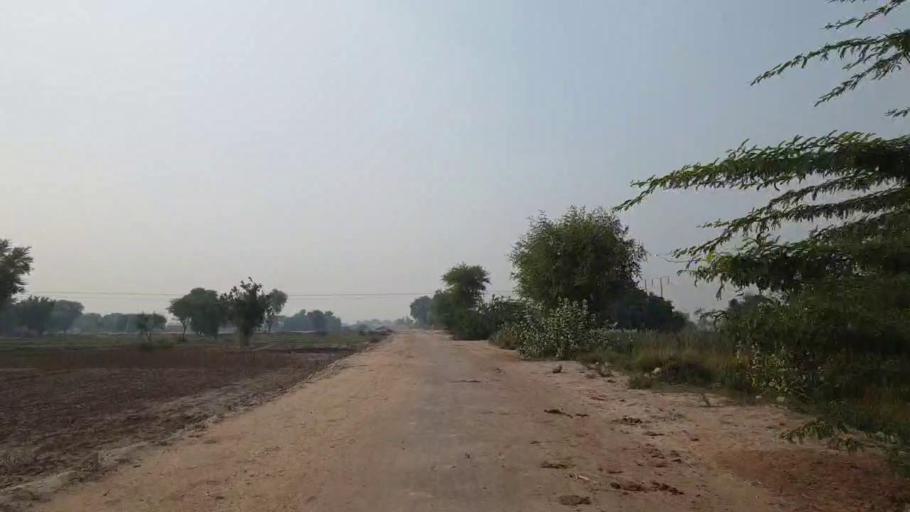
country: PK
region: Sindh
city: Bhan
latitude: 26.5416
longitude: 67.7151
